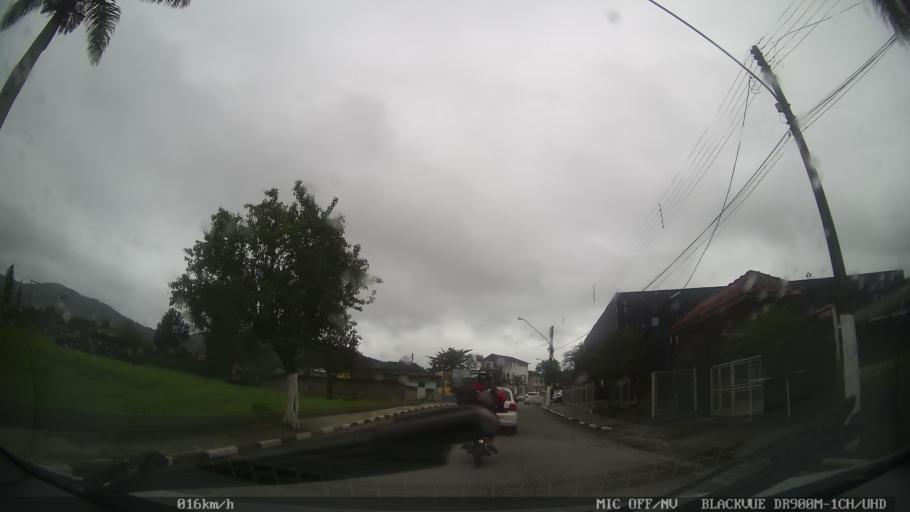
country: BR
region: Sao Paulo
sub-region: Juquia
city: Juquia
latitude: -24.3262
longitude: -47.6315
